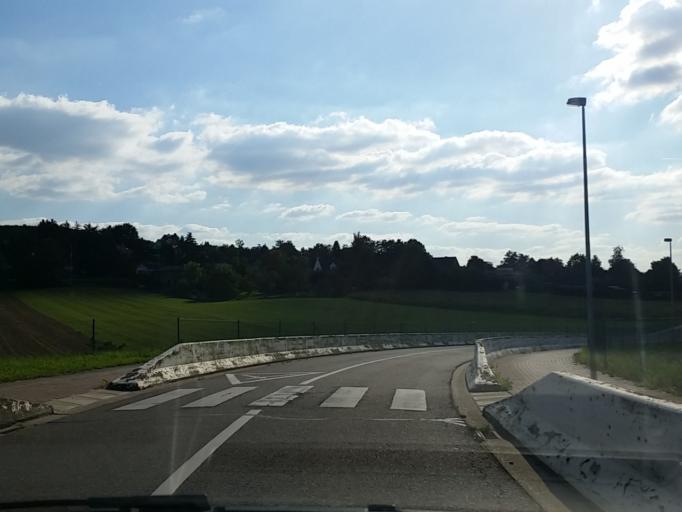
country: BE
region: Flanders
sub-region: Provincie Vlaams-Brabant
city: Bertem
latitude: 50.8987
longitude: 4.6164
